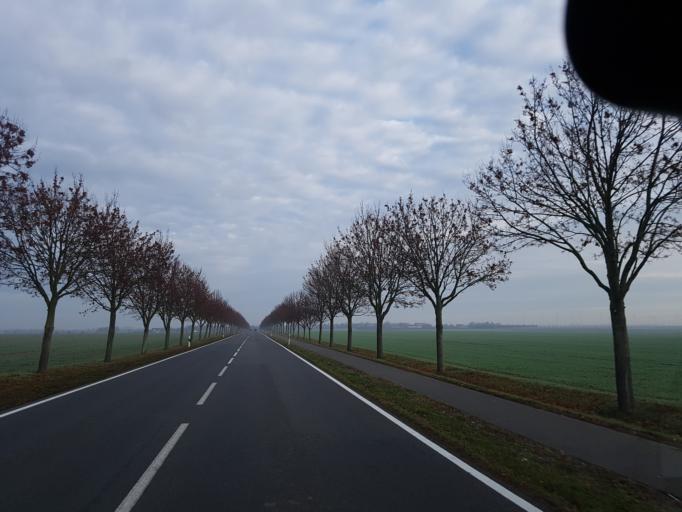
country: DE
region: Saxony-Anhalt
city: Kropstadt
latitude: 51.9887
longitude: 12.7672
